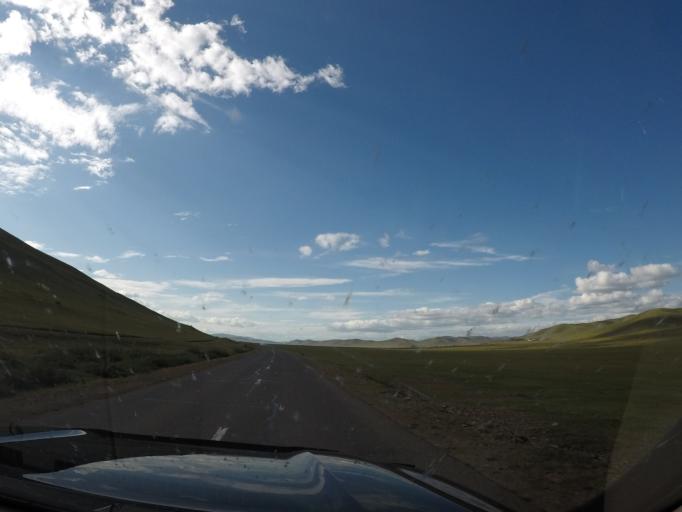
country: MN
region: Hentiy
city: Modot
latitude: 47.7008
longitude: 109.0755
